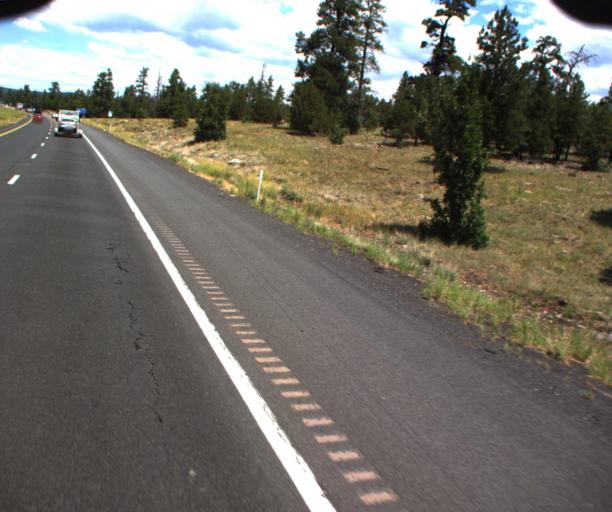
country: US
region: Arizona
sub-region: Coconino County
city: Sedona
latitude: 34.9177
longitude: -111.6420
